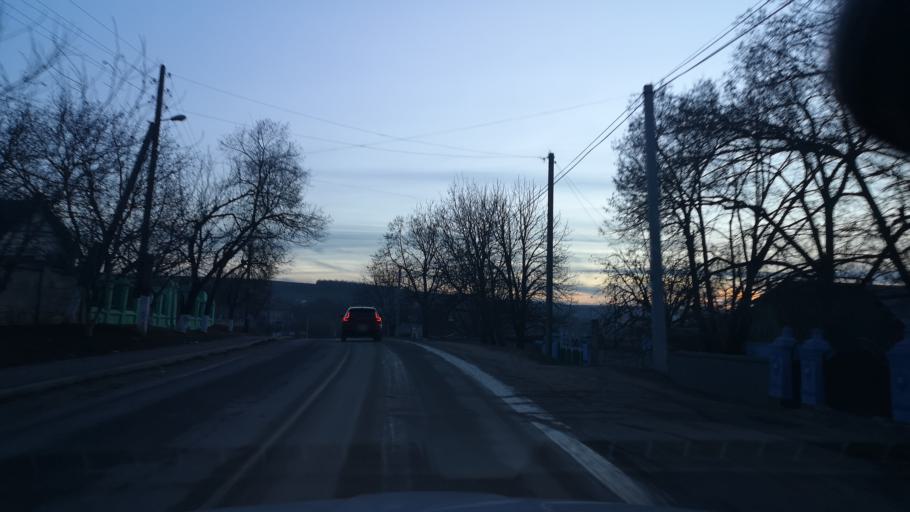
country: MD
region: Orhei
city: Orhei
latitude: 47.3084
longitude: 28.9305
